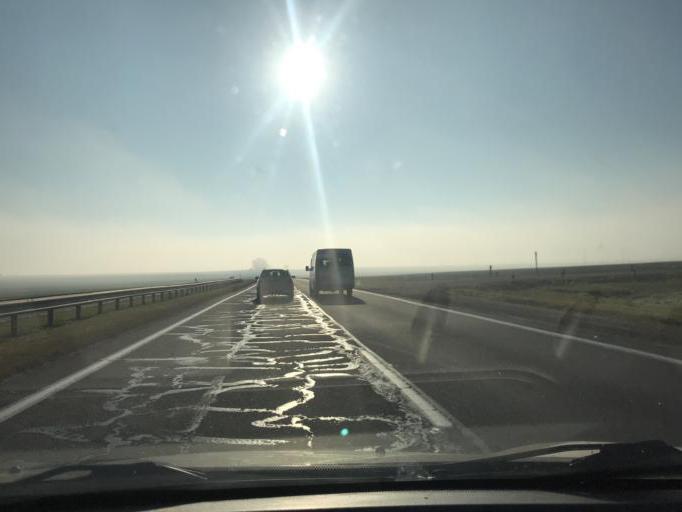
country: BY
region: Minsk
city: Dukora
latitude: 53.6941
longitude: 27.8972
